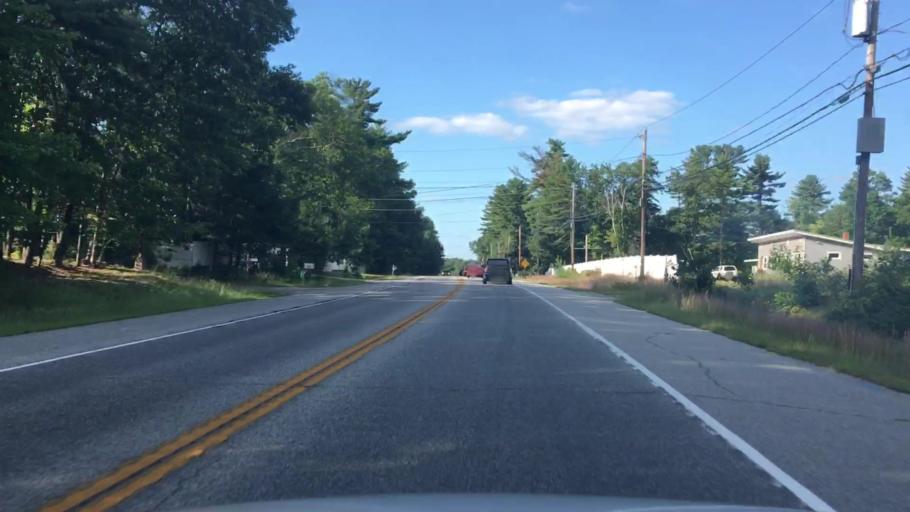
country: US
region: Maine
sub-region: Cumberland County
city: Raymond
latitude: 43.8694
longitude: -70.4650
